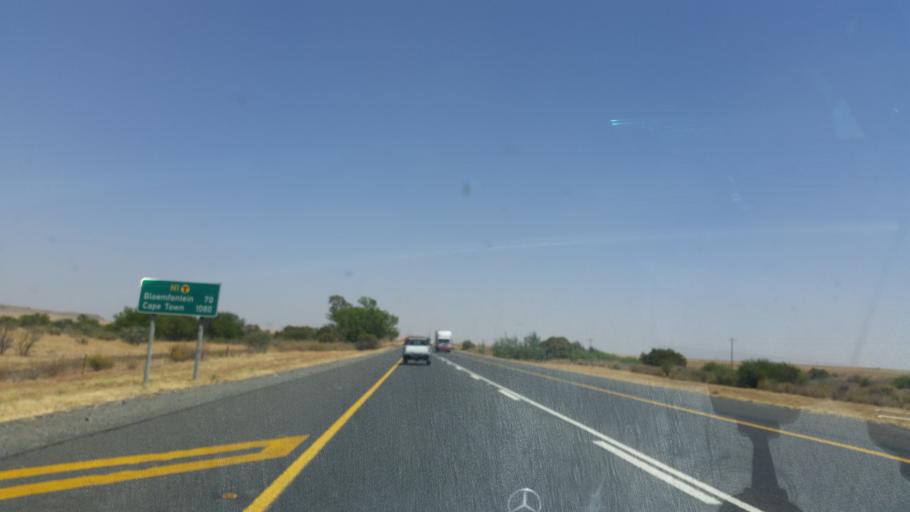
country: ZA
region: Orange Free State
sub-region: Lejweleputswa District Municipality
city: Brandfort
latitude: -28.7905
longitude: 26.7012
